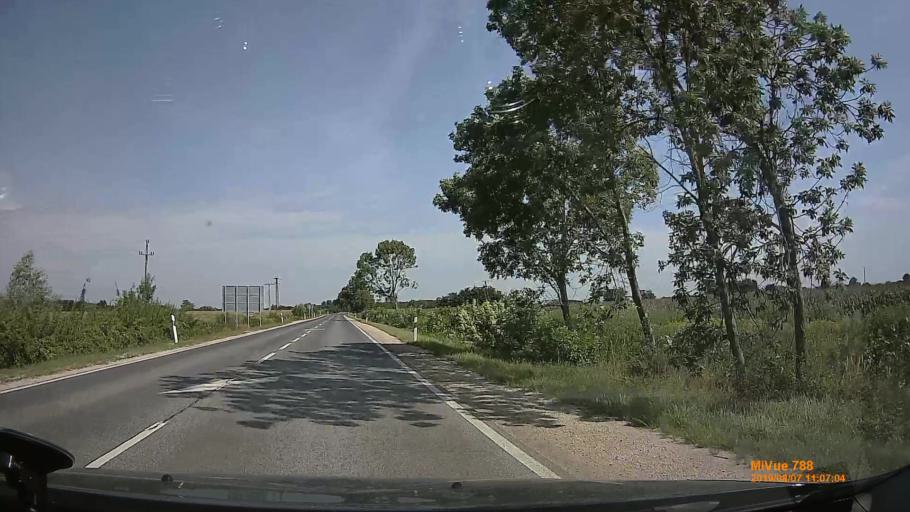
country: SI
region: Lendava-Lendva
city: Lendava
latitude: 46.6199
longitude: 16.4654
